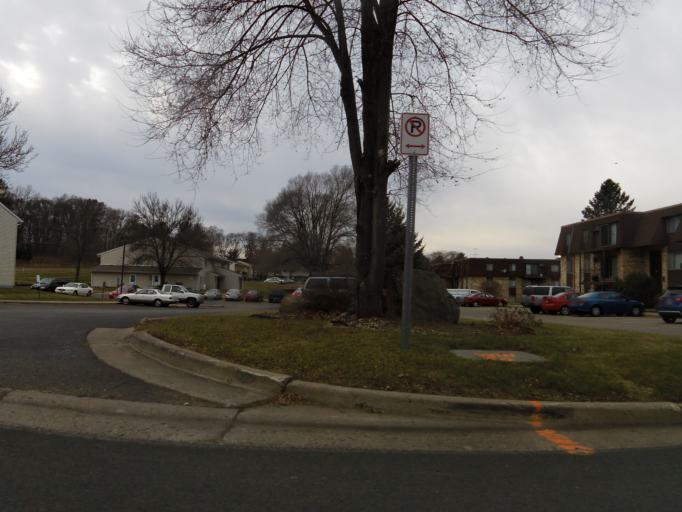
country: US
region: Wisconsin
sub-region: Pierce County
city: River Falls
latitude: 44.8544
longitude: -92.6091
